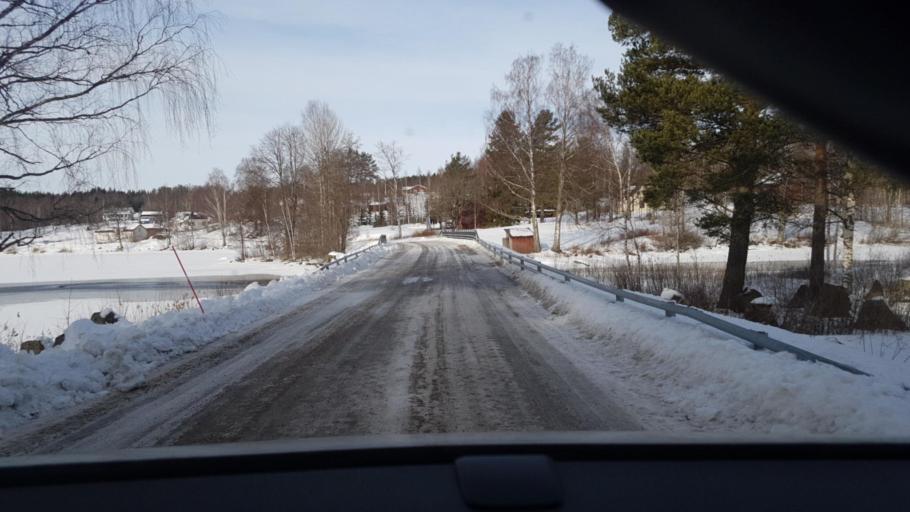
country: NO
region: Ostfold
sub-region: Romskog
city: Romskog
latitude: 59.8543
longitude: 11.9722
